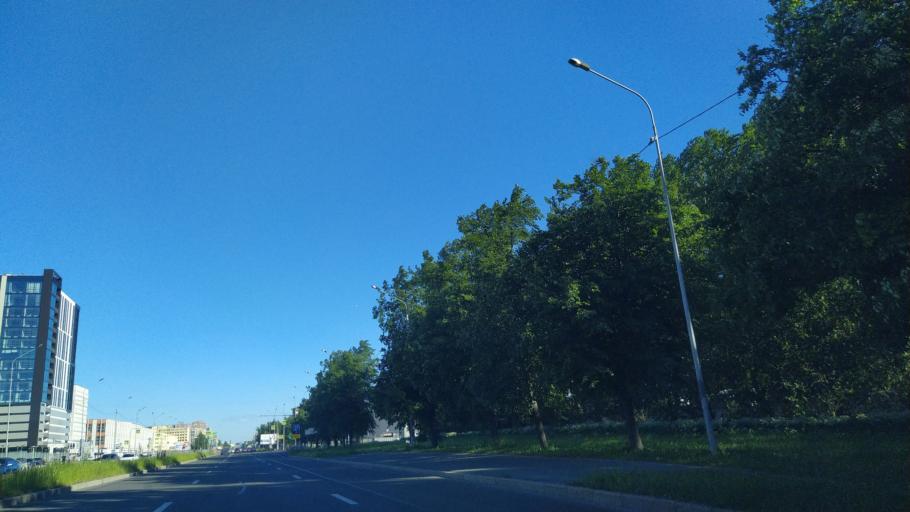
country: RU
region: St.-Petersburg
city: Kupchino
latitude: 59.8859
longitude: 30.3854
